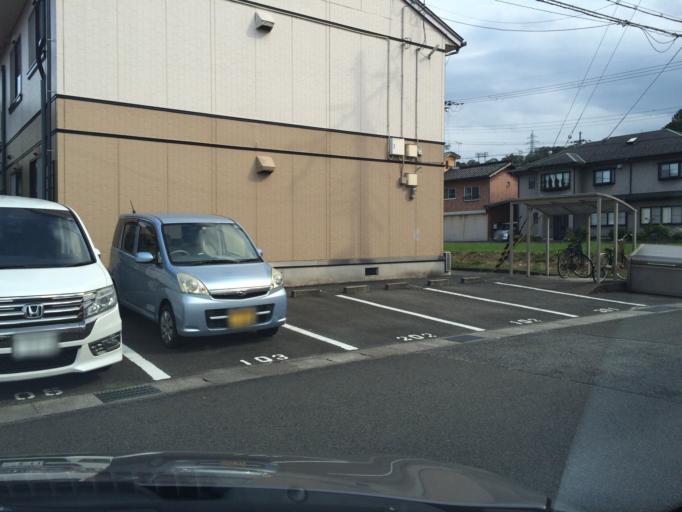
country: JP
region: Hyogo
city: Toyooka
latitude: 35.5363
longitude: 134.8092
